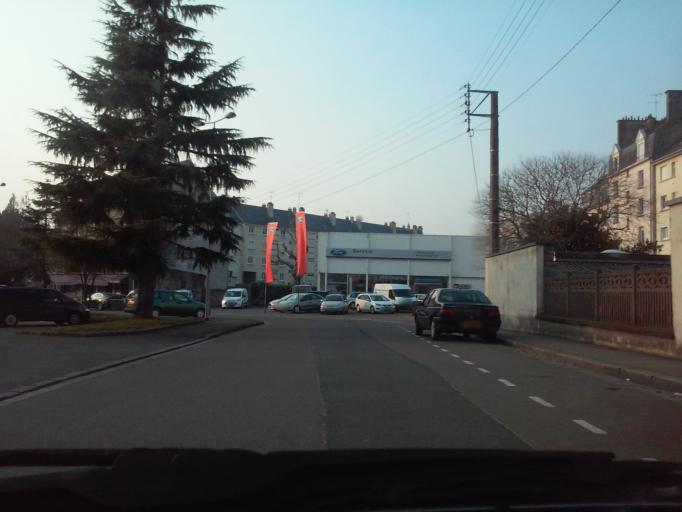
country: FR
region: Brittany
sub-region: Departement d'Ille-et-Vilaine
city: Fougeres
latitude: 48.3477
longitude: -1.1941
